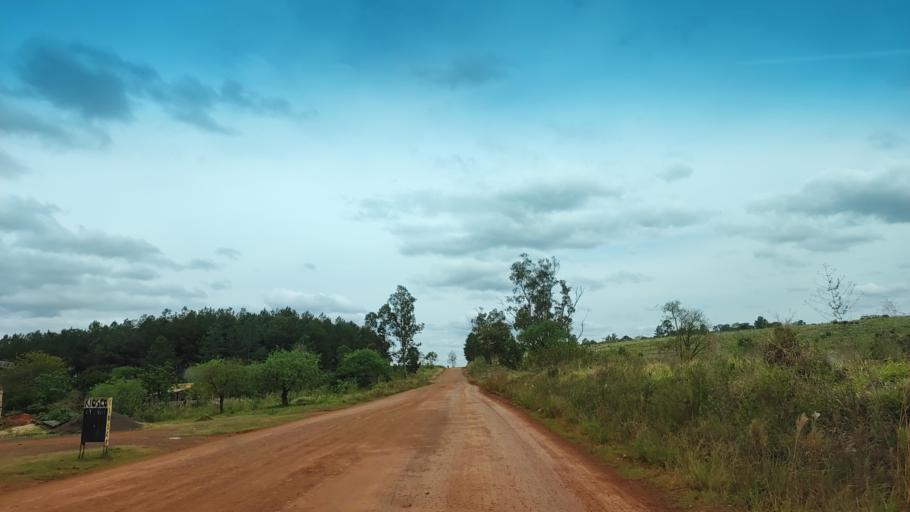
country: AR
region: Misiones
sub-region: Departamento de Capital
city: Posadas
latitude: -27.4800
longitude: -55.9708
